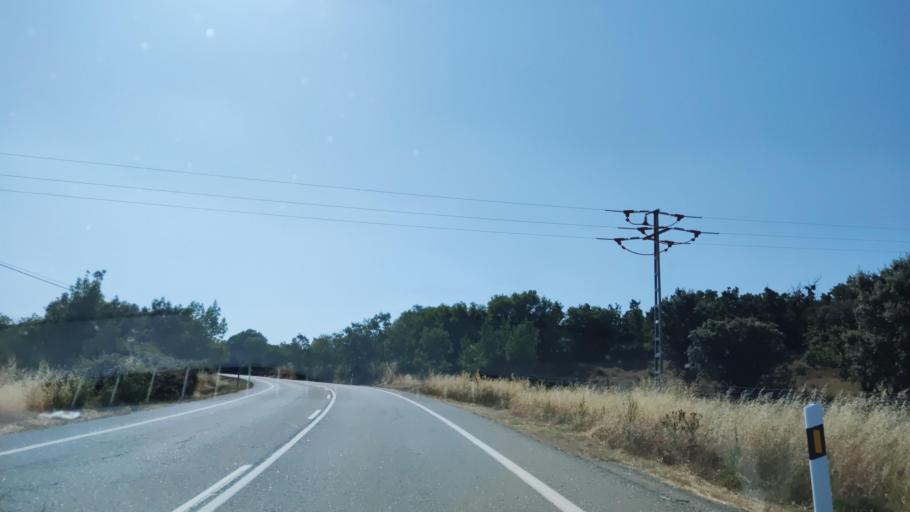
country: ES
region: Madrid
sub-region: Provincia de Madrid
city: Canencia
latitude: 40.9470
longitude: -3.7363
